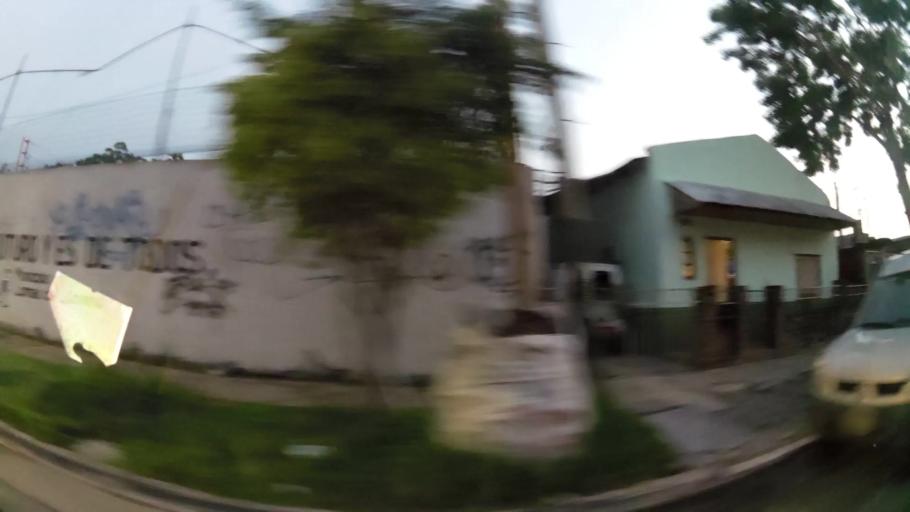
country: AR
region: Buenos Aires
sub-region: Partido de Lomas de Zamora
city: Lomas de Zamora
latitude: -34.7496
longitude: -58.3641
